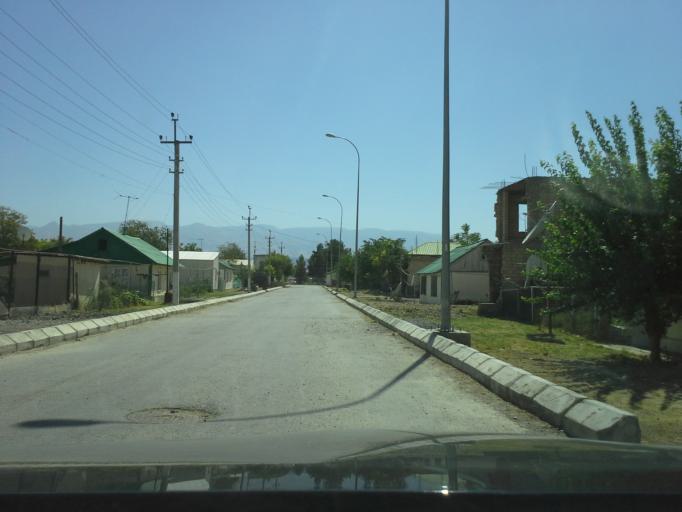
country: TM
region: Ahal
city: Ashgabat
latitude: 38.0049
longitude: 58.3030
